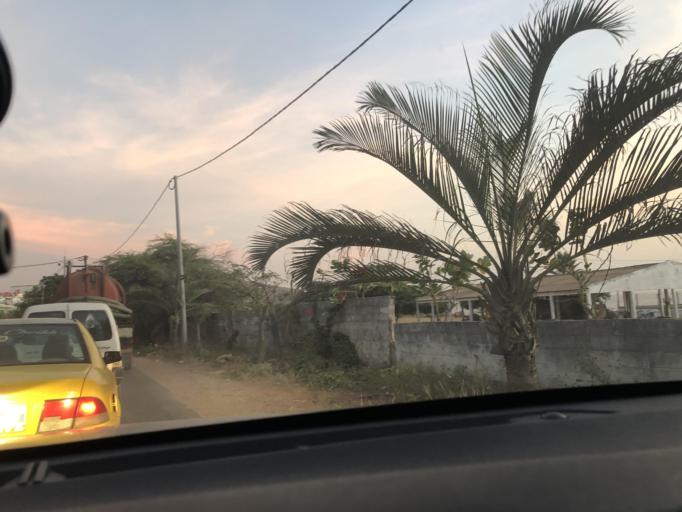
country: SN
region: Dakar
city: Mermoz Boabab
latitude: 14.7348
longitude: -17.5109
